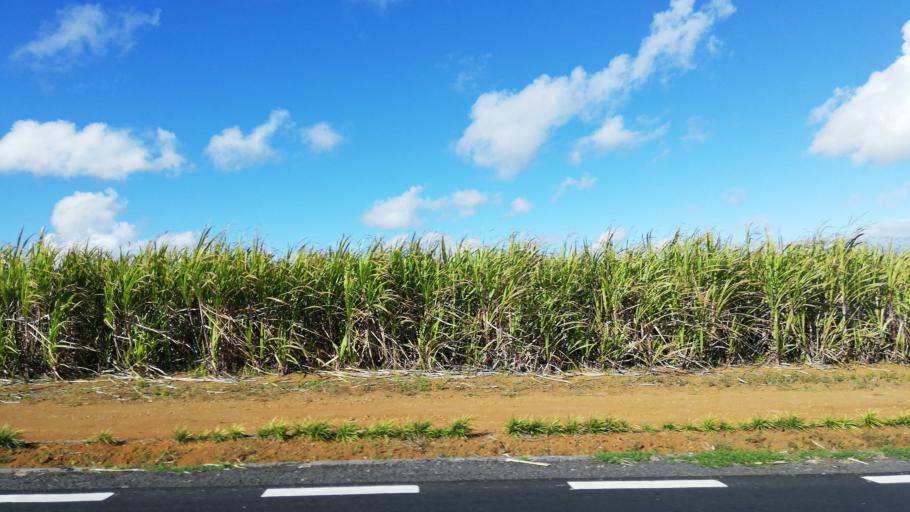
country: MU
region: Moka
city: La Dagotiere
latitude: -20.2340
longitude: 57.5672
